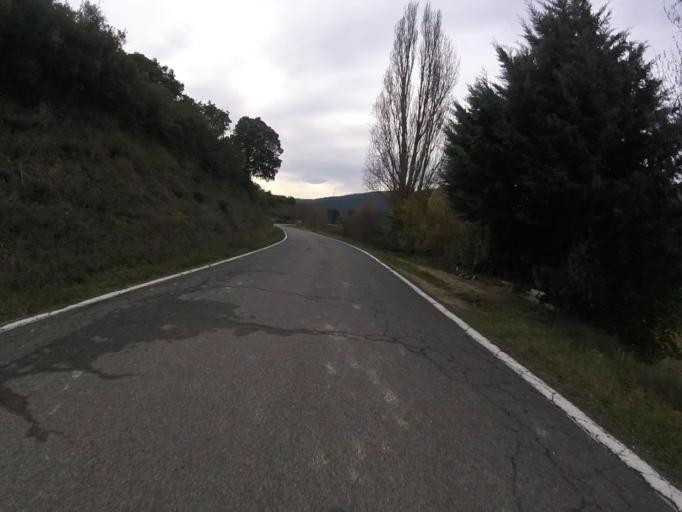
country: ES
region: Navarre
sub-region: Provincia de Navarra
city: Estella
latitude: 42.7047
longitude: -2.0524
